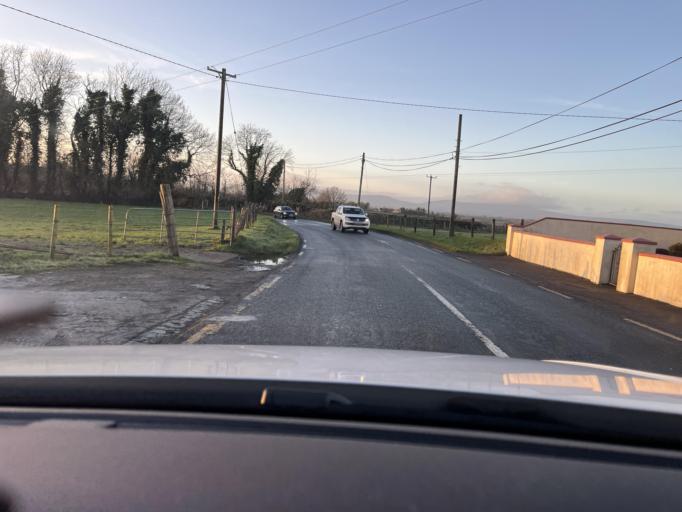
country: IE
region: Ulster
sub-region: An Cabhan
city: Ballyconnell
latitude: 54.0870
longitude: -7.6464
